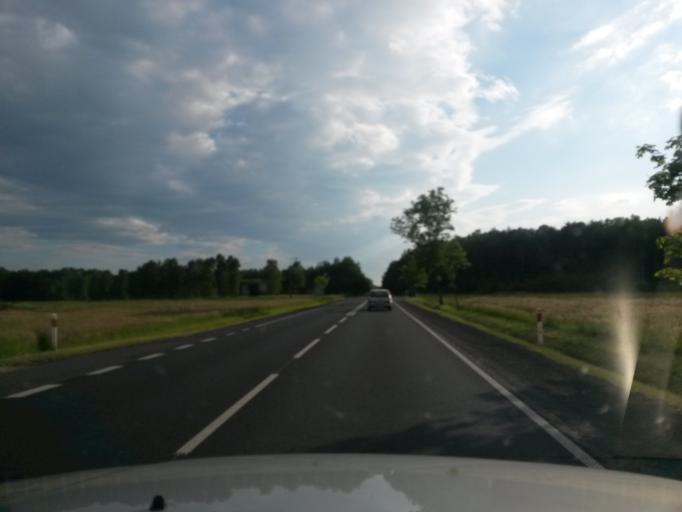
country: PL
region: Lodz Voivodeship
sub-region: Powiat belchatowski
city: Druzbice
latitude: 51.4052
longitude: 19.4456
